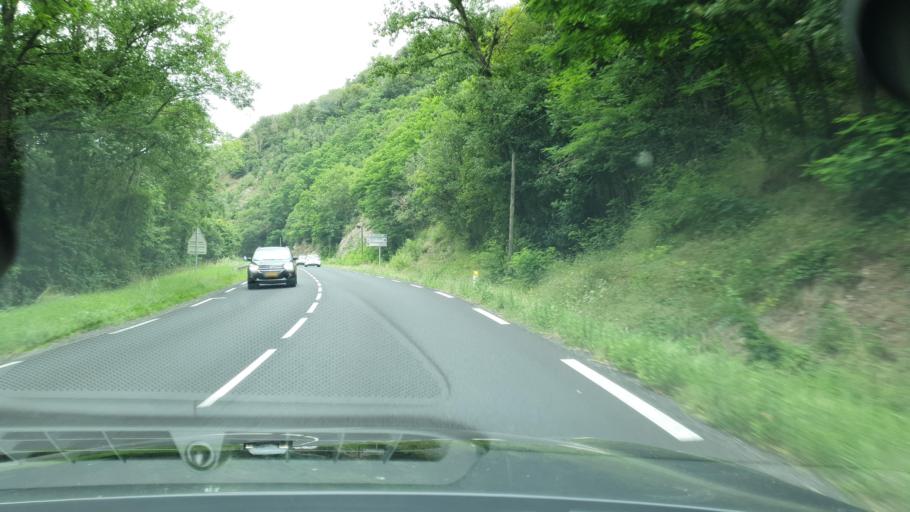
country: FR
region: Auvergne
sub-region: Departement du Puy-de-Dome
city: Champeix
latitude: 45.5739
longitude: 3.0616
